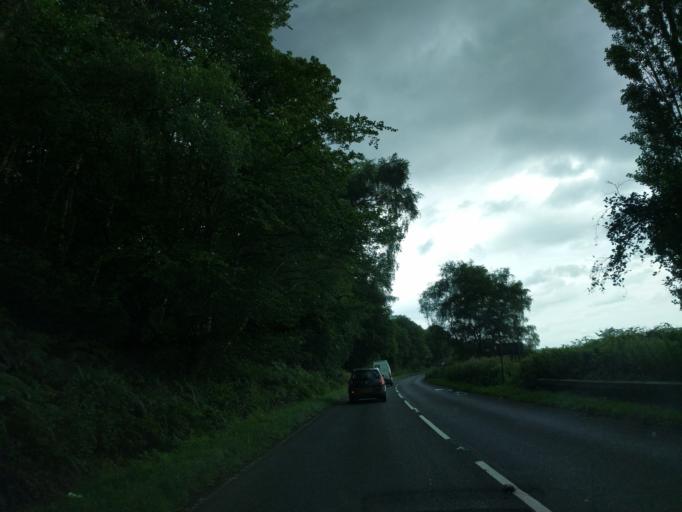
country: GB
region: England
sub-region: Staffordshire
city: Colwich
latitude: 52.7803
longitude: -1.9750
